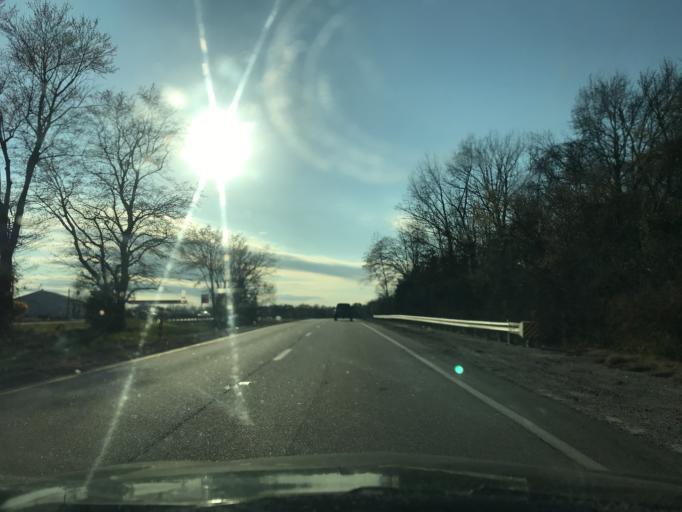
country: US
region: Virginia
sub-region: Prince Edward County
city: Farmville
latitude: 37.2741
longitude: -78.3015
